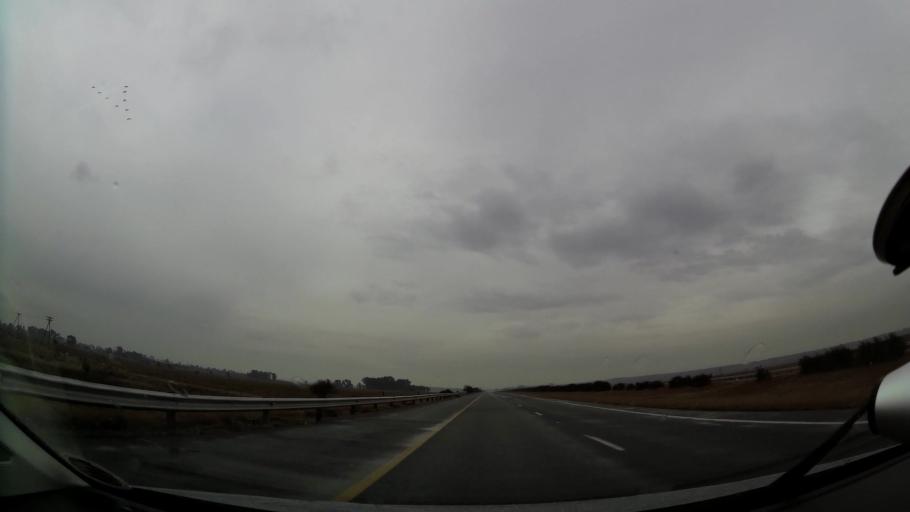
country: ZA
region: Gauteng
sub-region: Sedibeng District Municipality
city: Vanderbijlpark
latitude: -26.7180
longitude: 27.6969
